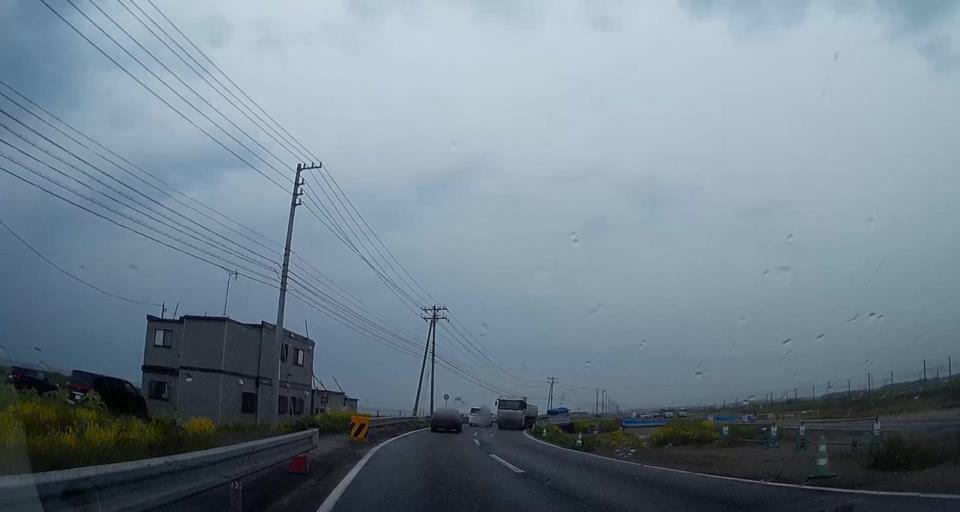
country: JP
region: Hokkaido
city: Shiraoi
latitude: 42.5891
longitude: 141.4504
